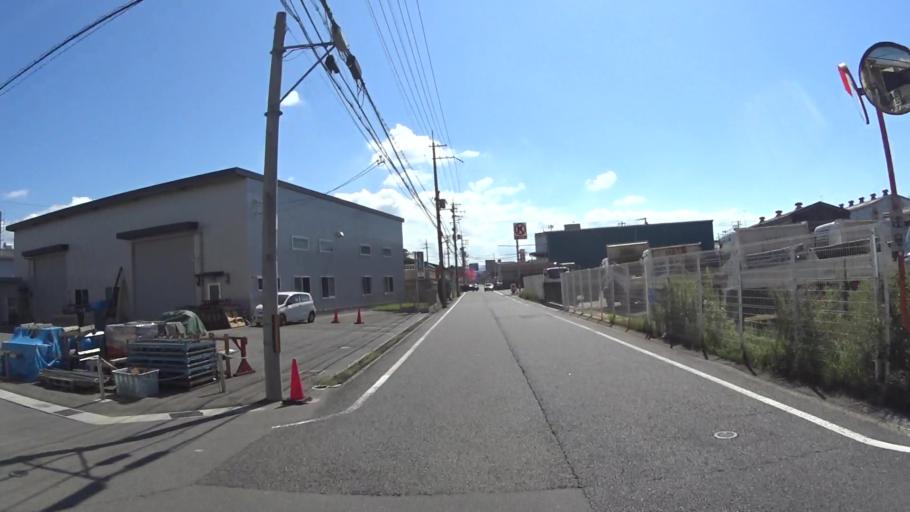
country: JP
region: Kyoto
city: Yawata
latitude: 34.8919
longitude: 135.7415
